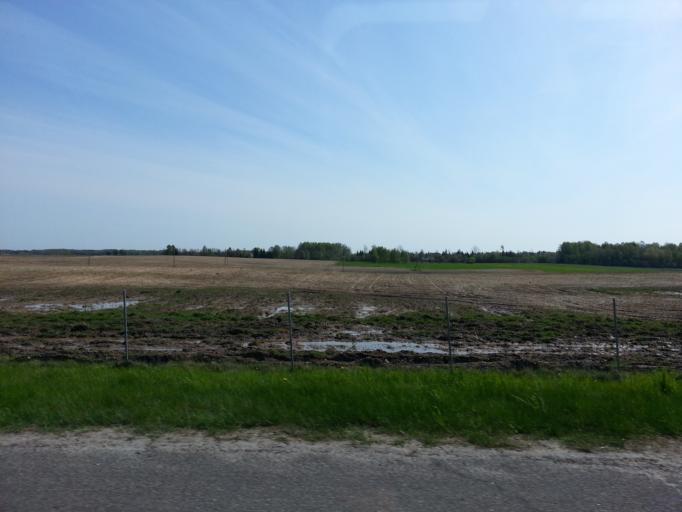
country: LT
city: Sirvintos
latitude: 55.1061
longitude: 24.8522
